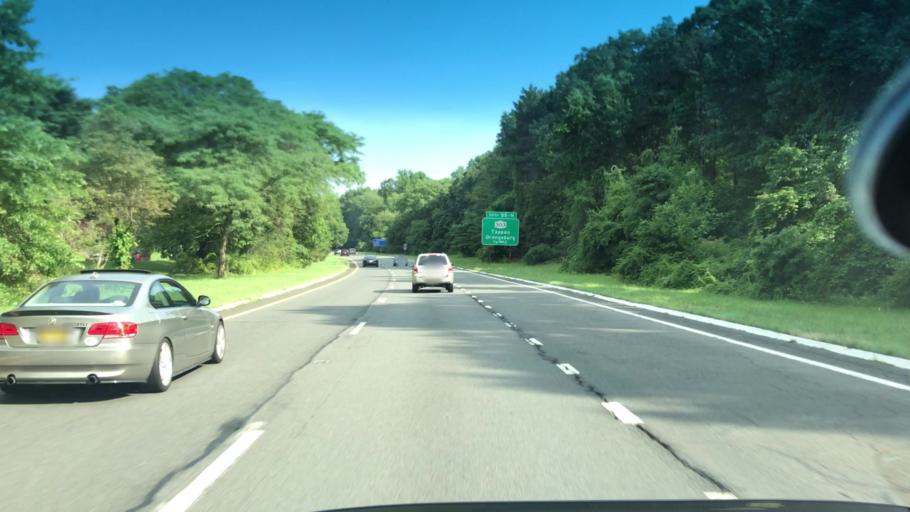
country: US
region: New York
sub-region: Rockland County
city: Orangeburg
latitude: 41.0419
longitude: -73.9562
